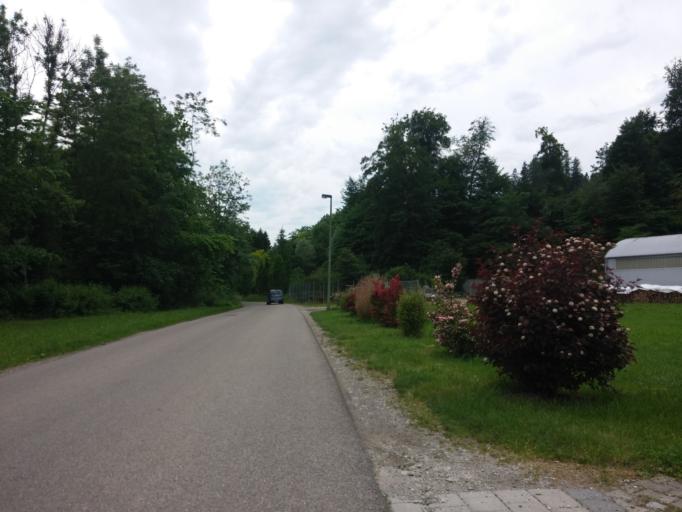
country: DE
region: Bavaria
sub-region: Swabia
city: Lautrach
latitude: 47.9015
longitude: 10.1145
